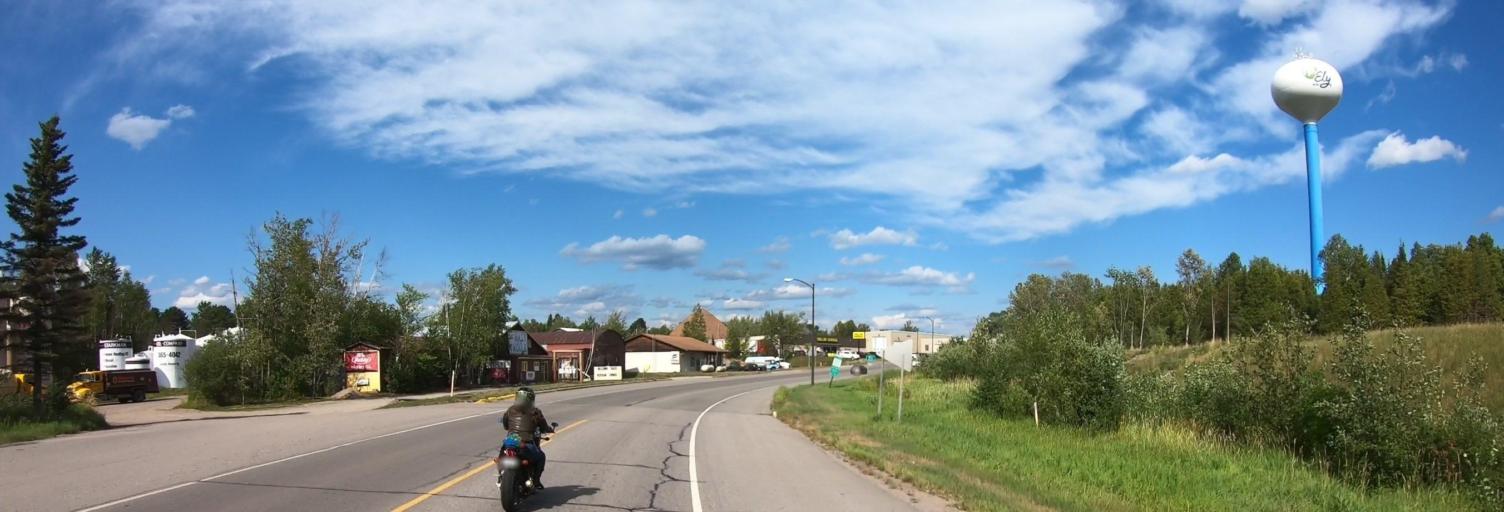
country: US
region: Minnesota
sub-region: Saint Louis County
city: Ely
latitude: 47.9024
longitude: -91.8751
